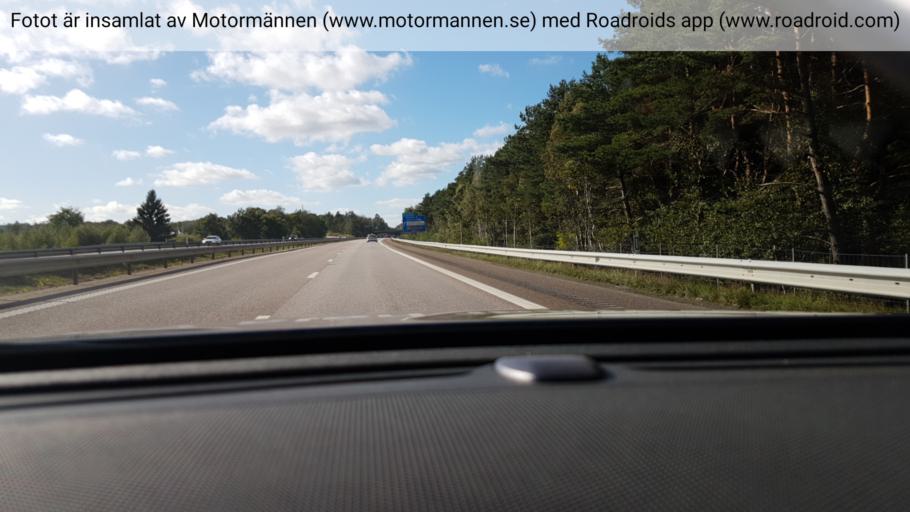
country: SE
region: Vaestra Goetaland
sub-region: Harryda Kommun
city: Molnlycke
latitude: 57.6713
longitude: 12.1039
